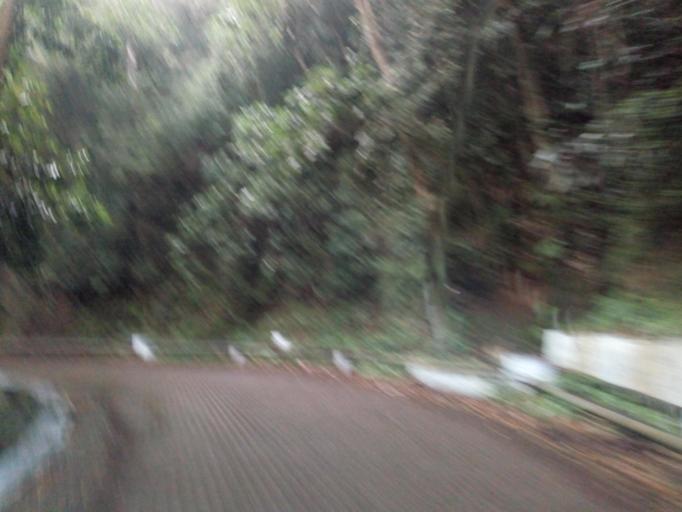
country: IN
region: Tamil Nadu
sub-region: Nilgiri
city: Wellington
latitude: 11.3511
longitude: 76.8265
